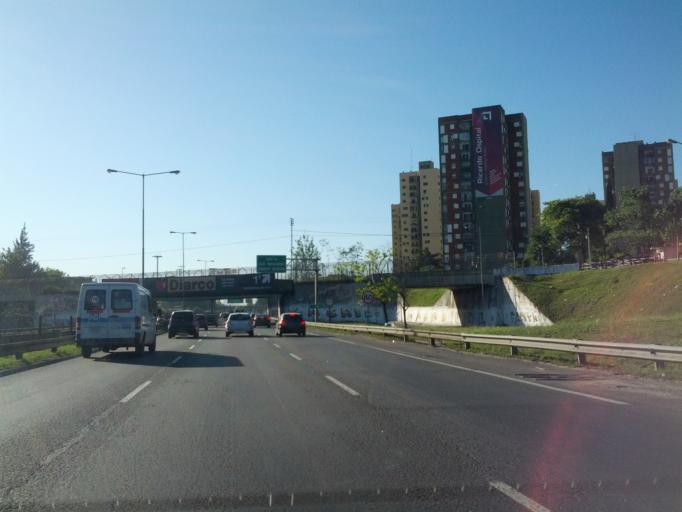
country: AR
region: Buenos Aires F.D.
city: Villa Lugano
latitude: -34.6828
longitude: -58.4909
